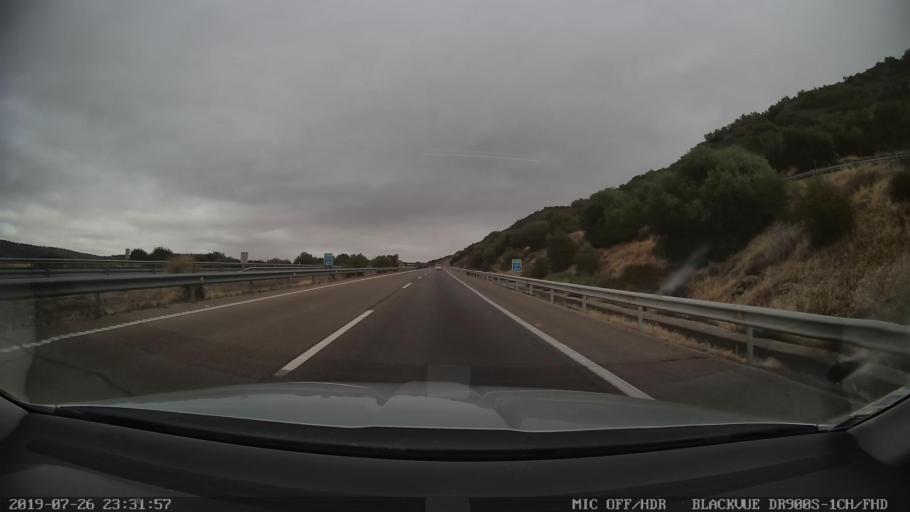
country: ES
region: Extremadura
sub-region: Provincia de Caceres
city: Puerto de Santa Cruz
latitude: 39.3093
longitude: -5.8570
